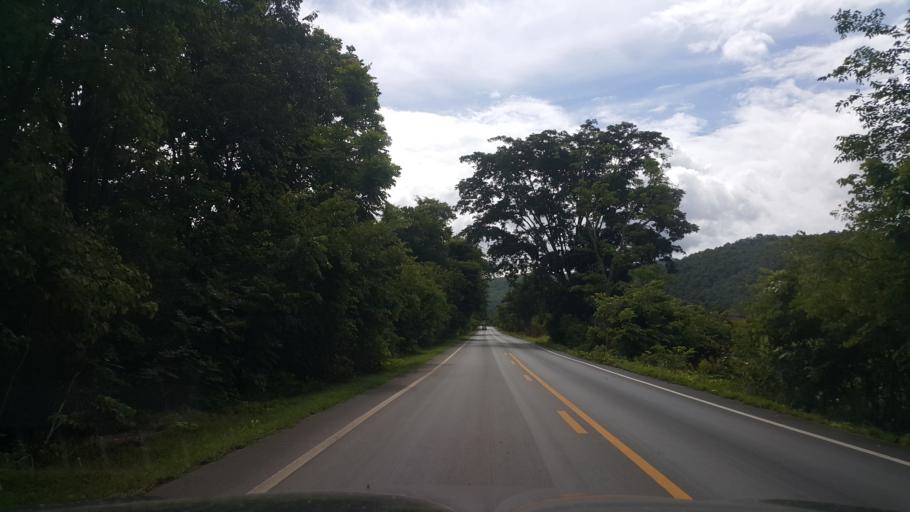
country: TH
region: Uttaradit
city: Thong Saen Khan
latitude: 17.3796
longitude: 100.2762
